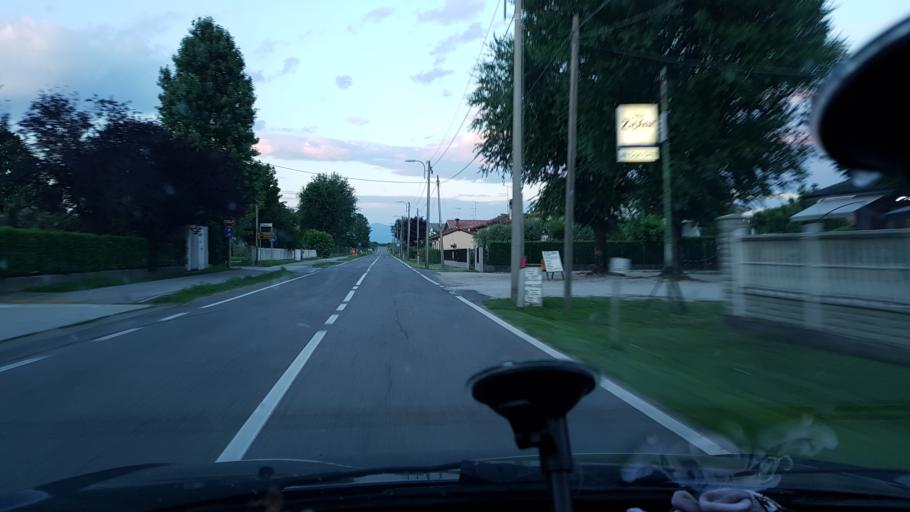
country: IT
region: Friuli Venezia Giulia
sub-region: Provincia di Gorizia
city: Romans d'Isonzo
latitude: 45.8909
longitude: 13.4521
